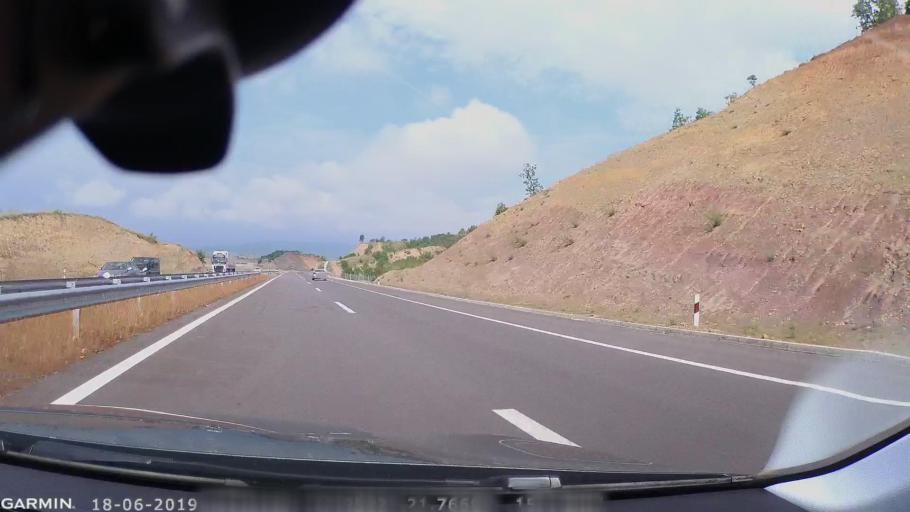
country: MK
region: Sveti Nikole
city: Gorobinci
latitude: 41.9238
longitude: 21.8444
